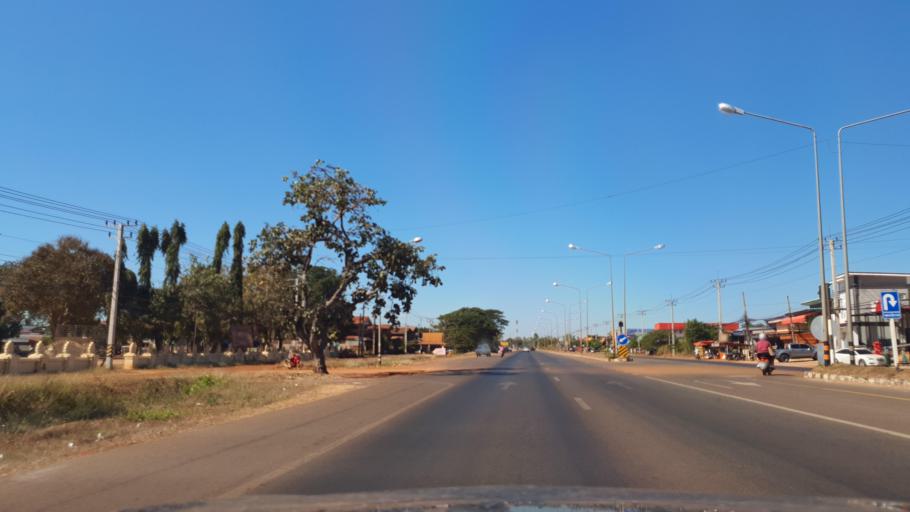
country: TH
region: Sakon Nakhon
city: Sakon Nakhon
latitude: 17.2637
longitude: 104.1315
